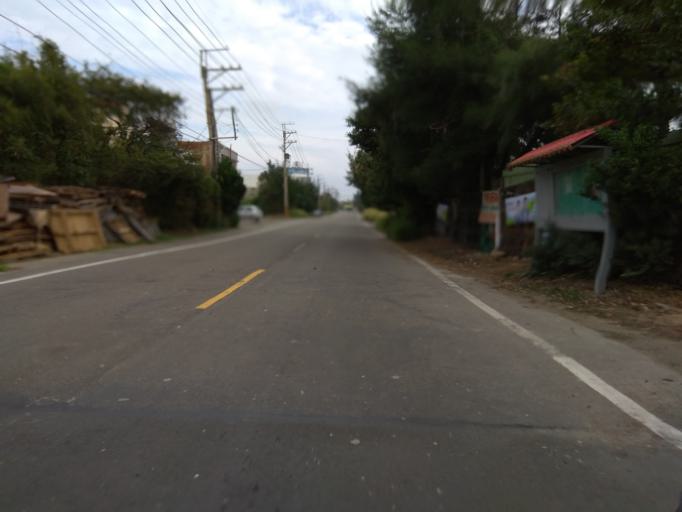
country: TW
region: Taiwan
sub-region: Hsinchu
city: Zhubei
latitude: 24.9844
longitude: 121.0411
